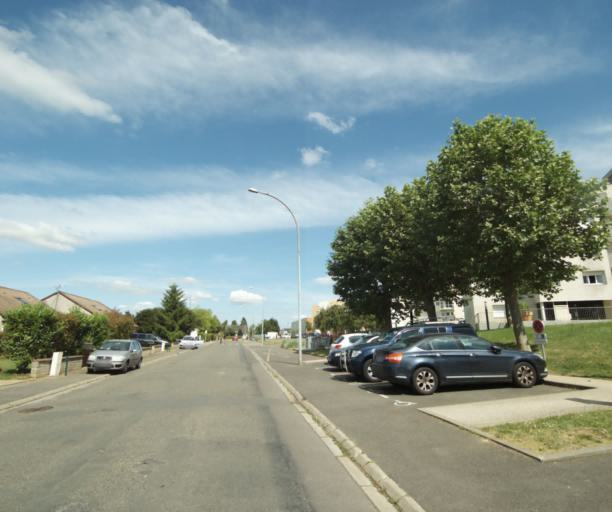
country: FR
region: Centre
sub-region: Departement d'Eure-et-Loir
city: Mainvilliers
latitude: 48.4381
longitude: 1.4448
